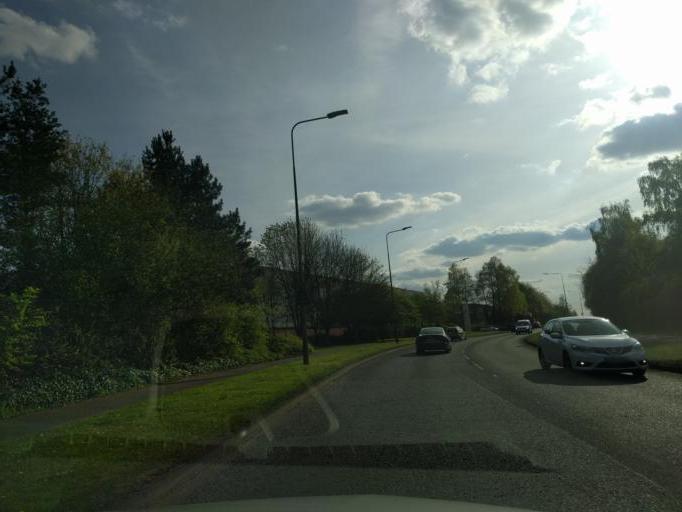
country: GB
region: England
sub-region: Suffolk
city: Great Barton
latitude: 52.2425
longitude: 0.7487
